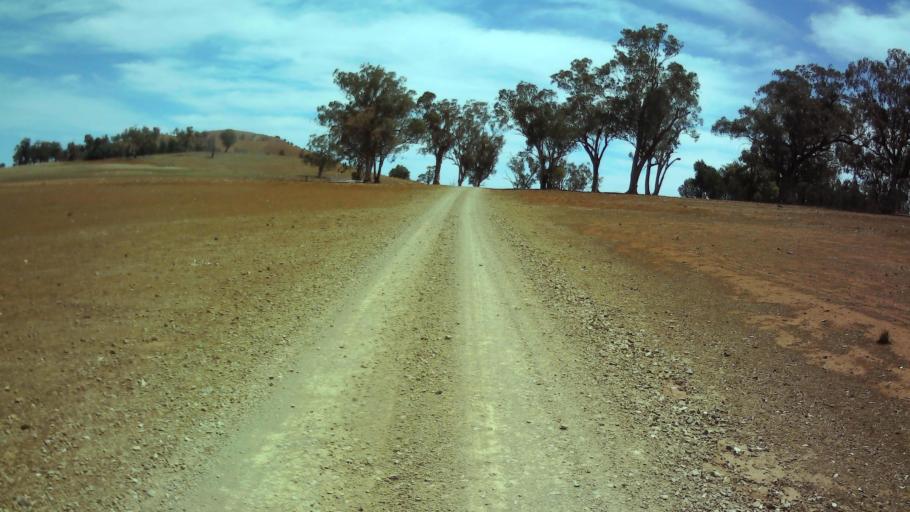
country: AU
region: New South Wales
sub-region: Weddin
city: Grenfell
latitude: -33.7465
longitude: 148.1700
